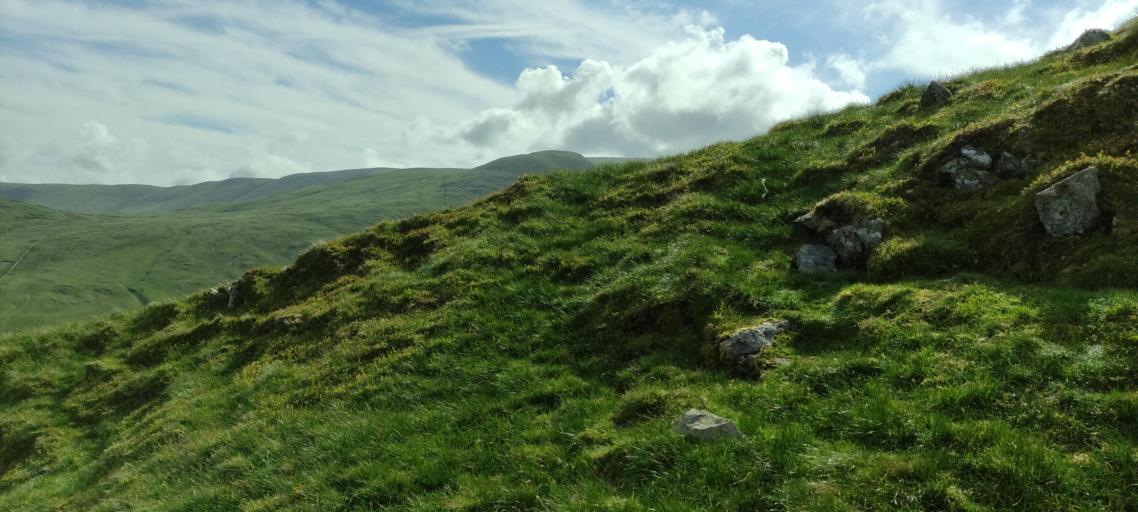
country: GB
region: England
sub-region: Cumbria
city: Ambleside
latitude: 54.5037
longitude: -2.8909
